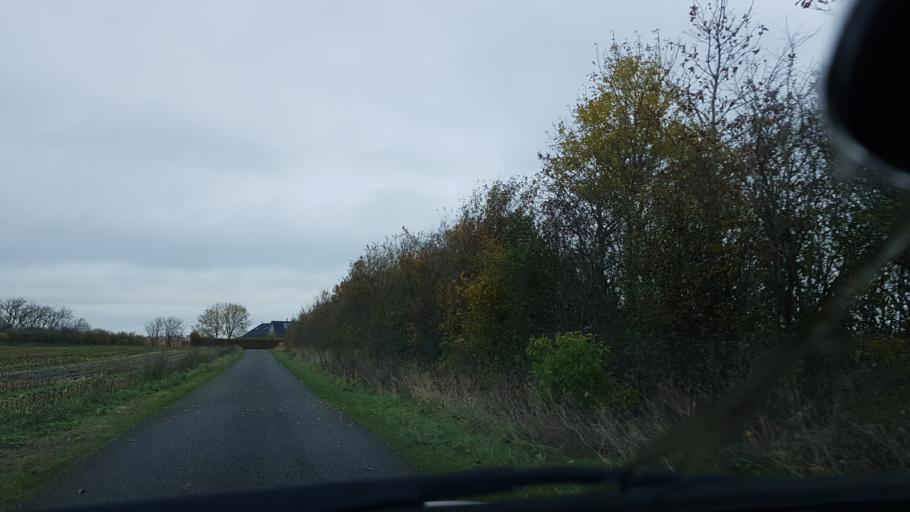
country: DK
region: South Denmark
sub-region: Esbjerg Kommune
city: Ribe
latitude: 55.2593
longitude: 8.8375
